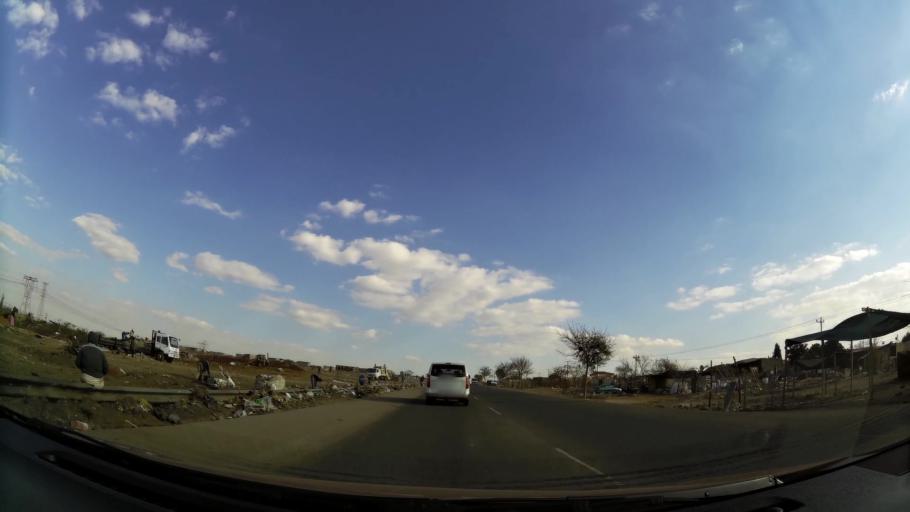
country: ZA
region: Gauteng
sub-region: Ekurhuleni Metropolitan Municipality
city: Tembisa
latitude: -25.9938
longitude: 28.1888
